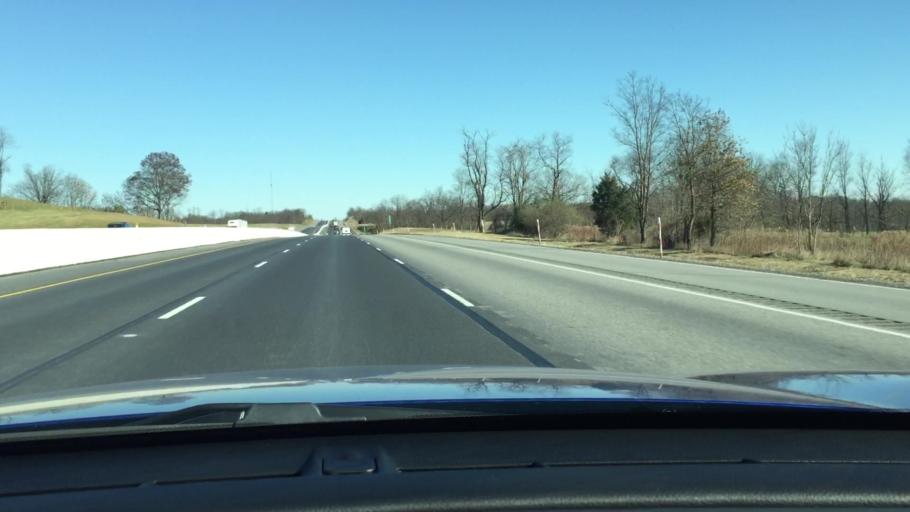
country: US
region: Pennsylvania
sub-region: Cumberland County
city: Shippensburg
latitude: 40.1760
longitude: -77.5314
